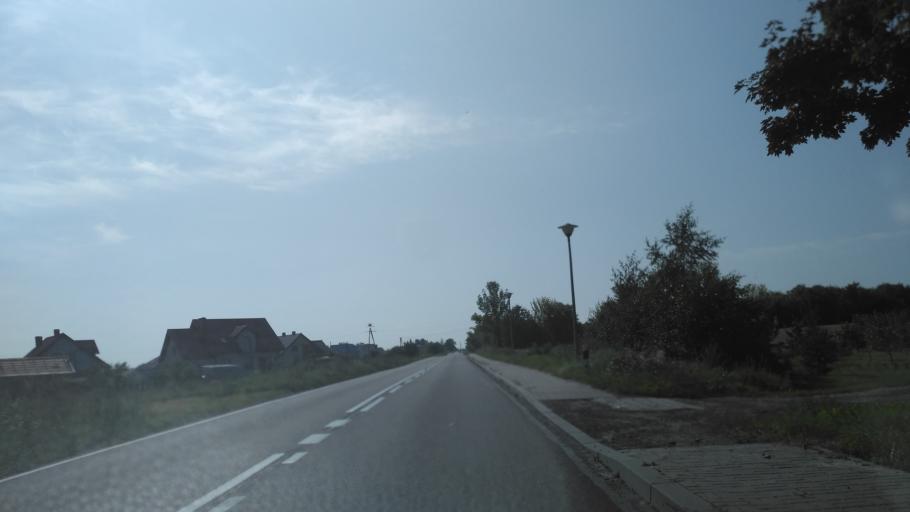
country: PL
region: Lublin Voivodeship
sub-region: Powiat chelmski
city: Rejowiec Fabryczny
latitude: 51.1889
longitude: 23.1645
